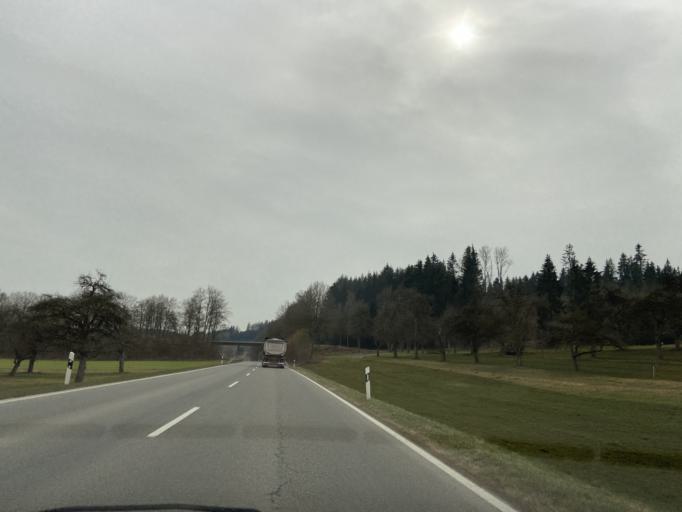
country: DE
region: Baden-Wuerttemberg
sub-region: Tuebingen Region
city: Ostrach
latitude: 47.9736
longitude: 9.3464
